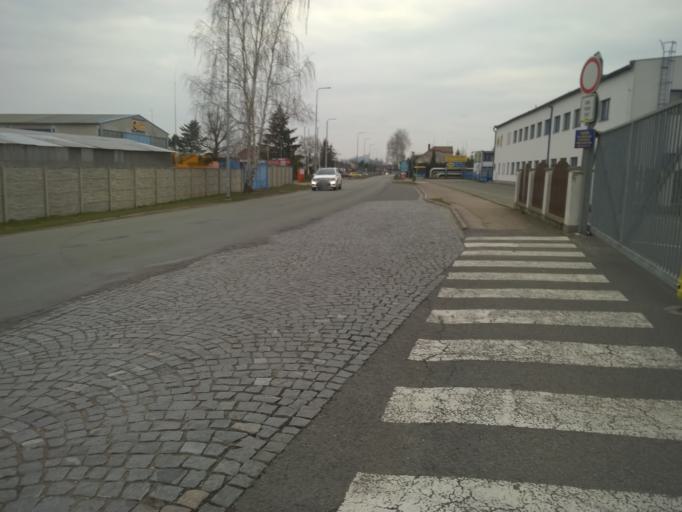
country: CZ
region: Pardubicky
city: Stare Hradiste
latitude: 50.0627
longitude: 15.7657
